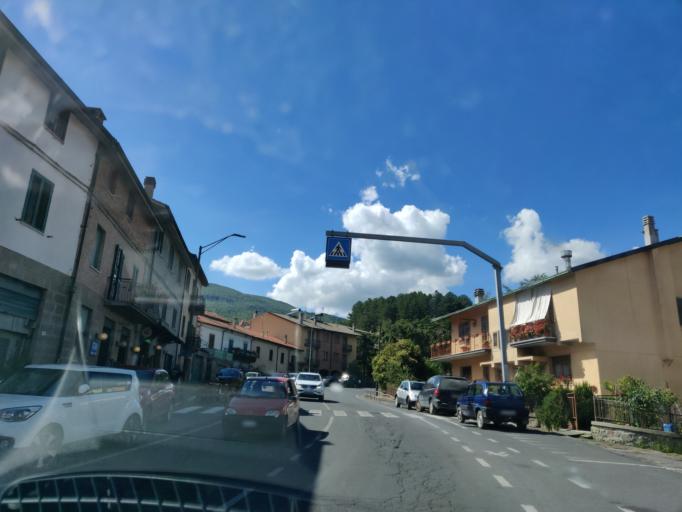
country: IT
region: Tuscany
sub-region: Provincia di Siena
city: Abbadia San Salvatore
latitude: 42.8840
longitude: 11.6710
